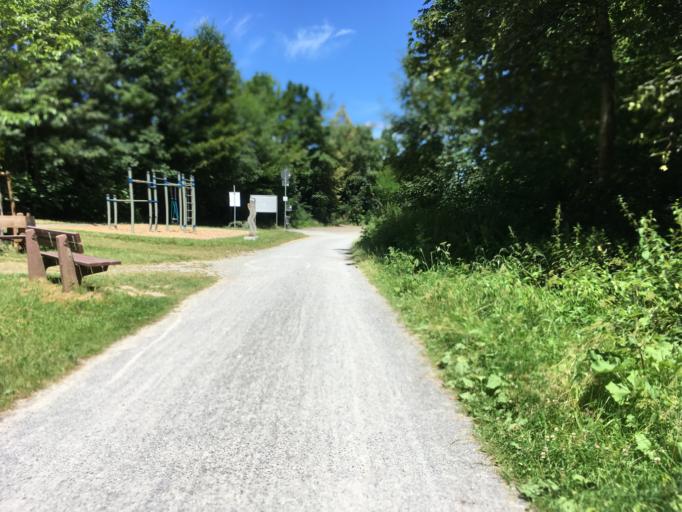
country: DE
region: Baden-Wuerttemberg
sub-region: Regierungsbezirk Stuttgart
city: Vaihingen an der Enz
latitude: 48.9198
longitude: 8.9508
